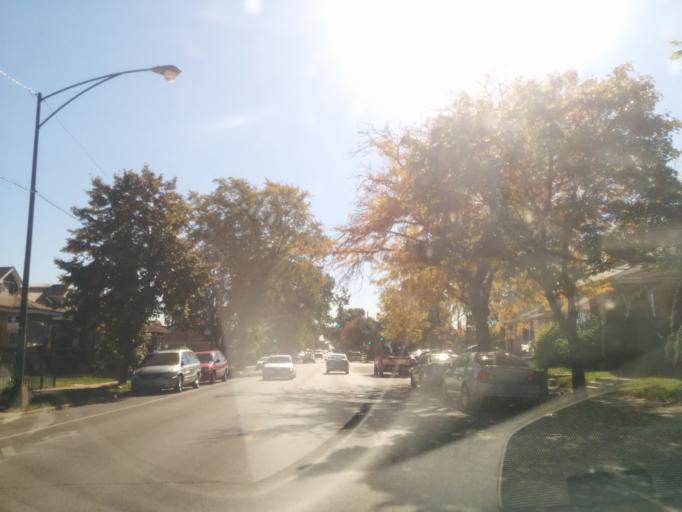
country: US
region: Illinois
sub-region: Cook County
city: Elmwood Park
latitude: 41.9355
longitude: -87.7857
